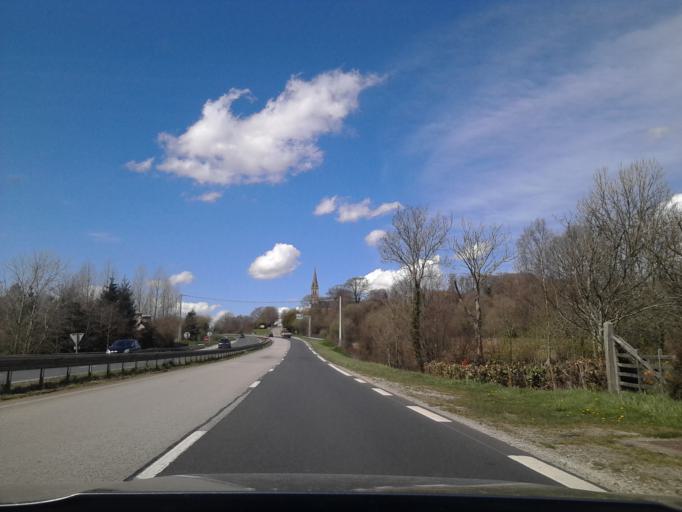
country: FR
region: Lower Normandy
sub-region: Departement de la Manche
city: Valognes
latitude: 49.5299
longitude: -1.5195
